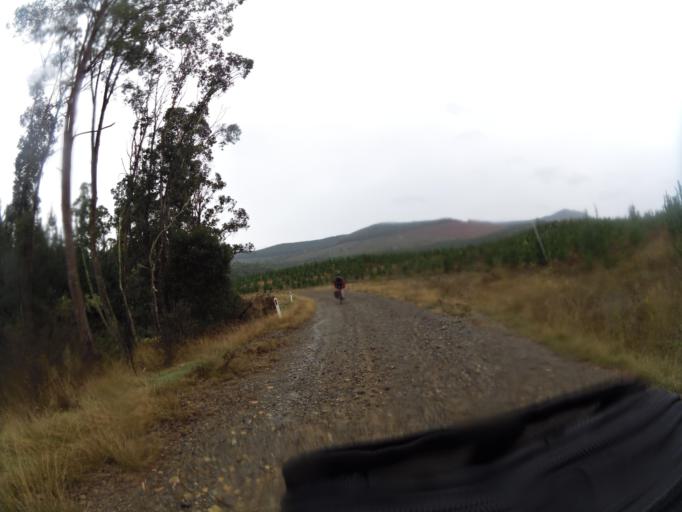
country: AU
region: New South Wales
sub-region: Greater Hume Shire
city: Holbrook
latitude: -36.2143
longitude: 147.5682
